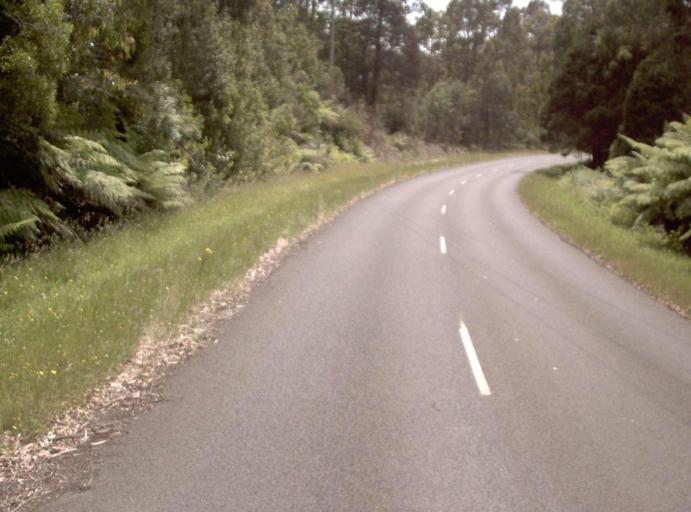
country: AU
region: Victoria
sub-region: Latrobe
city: Moe
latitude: -37.8622
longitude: 146.3871
